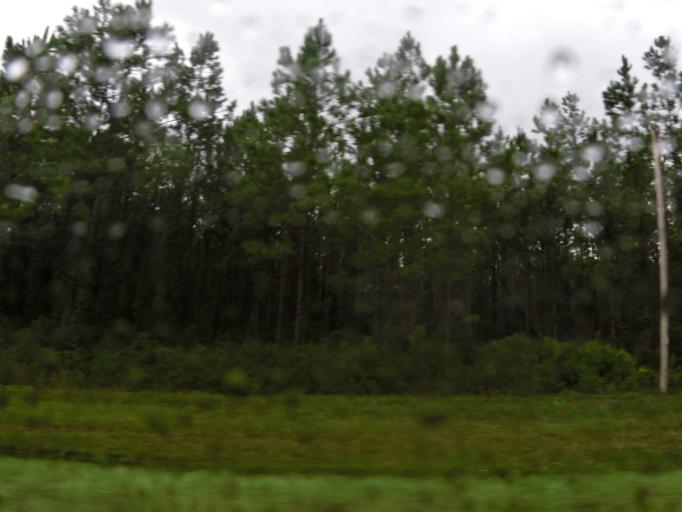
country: US
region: Florida
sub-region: Nassau County
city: Callahan
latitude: 30.5227
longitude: -81.9934
